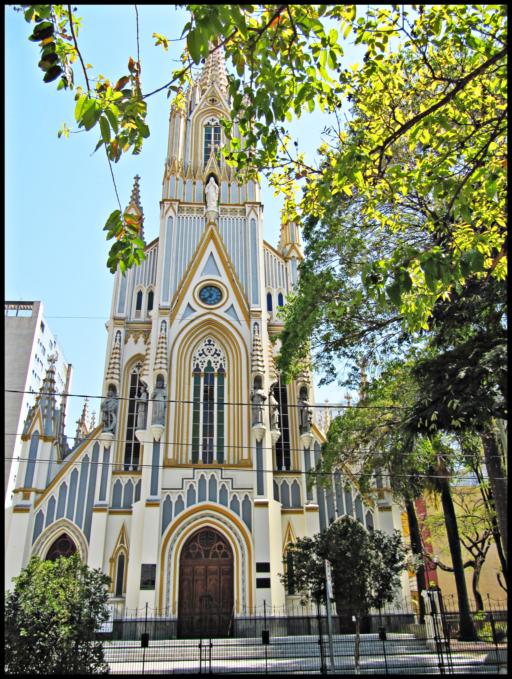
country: BR
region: Minas Gerais
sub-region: Belo Horizonte
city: Belo Horizonte
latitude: -19.9288
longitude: -43.9385
